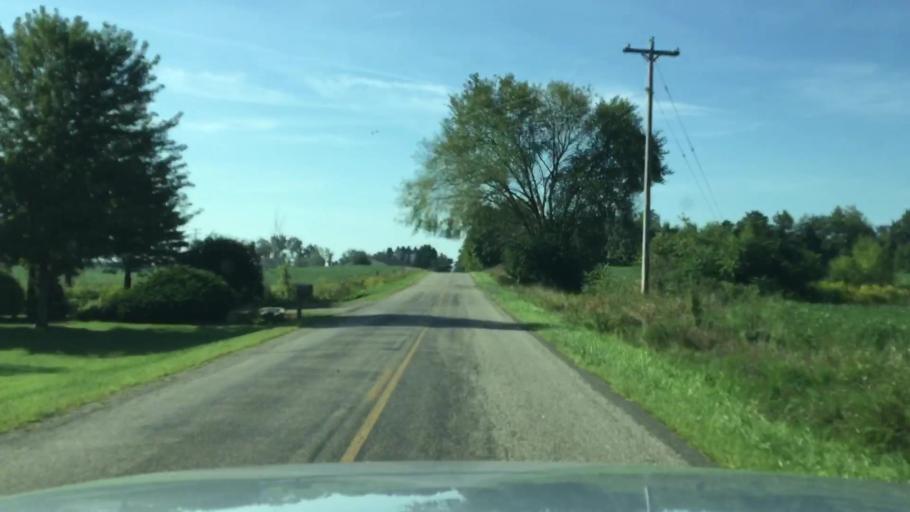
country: US
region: Michigan
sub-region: Lenawee County
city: Hudson
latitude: 41.9043
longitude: -84.4204
